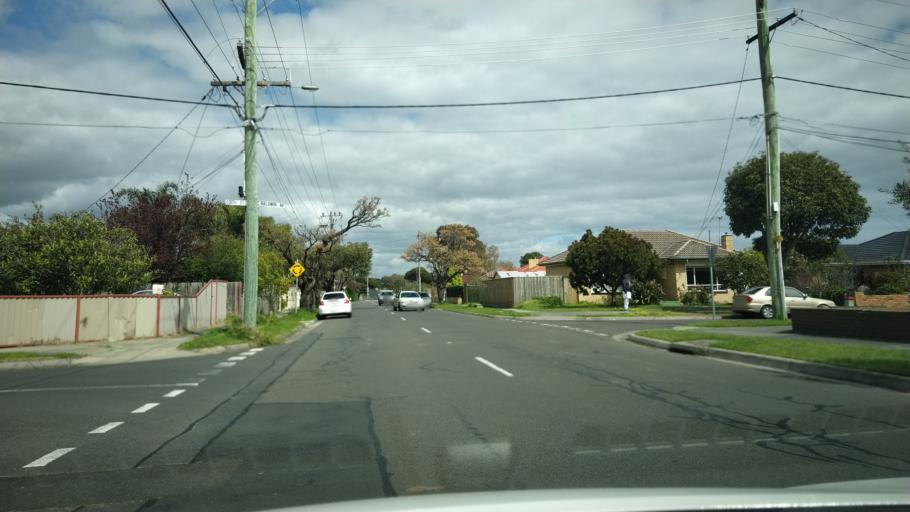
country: AU
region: Victoria
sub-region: Greater Dandenong
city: Noble Park
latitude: -37.9755
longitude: 145.1784
